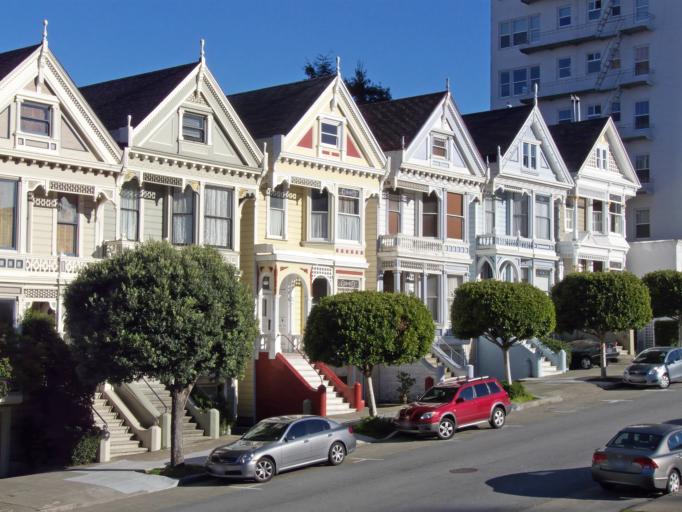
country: US
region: California
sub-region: San Francisco County
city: San Francisco
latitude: 37.7767
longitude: -122.4335
